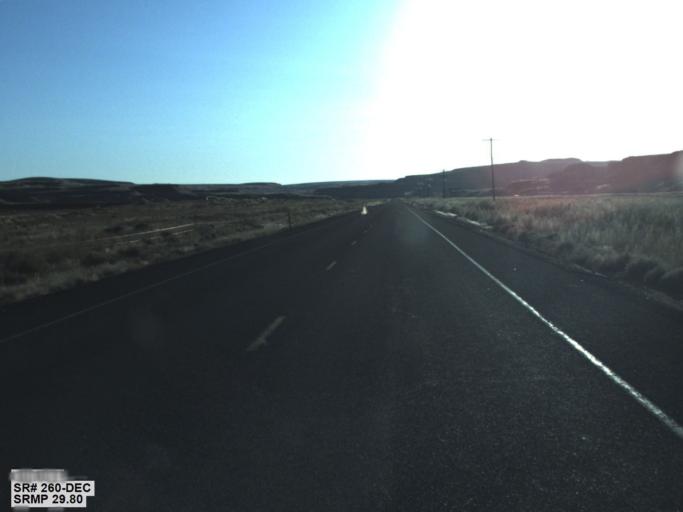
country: US
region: Washington
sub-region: Franklin County
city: Connell
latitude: 46.6726
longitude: -118.4660
